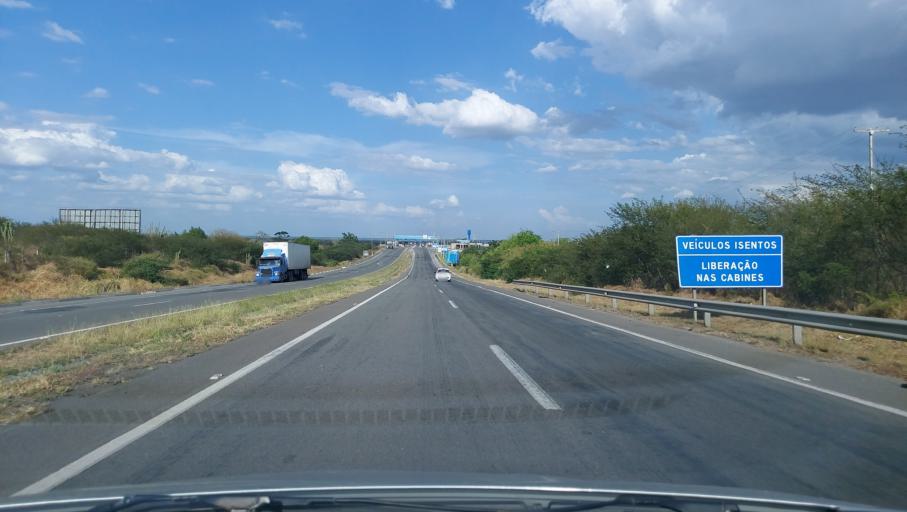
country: BR
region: Bahia
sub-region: Santo Estevao
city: Santo Estevao
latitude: -12.5343
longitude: -39.4198
